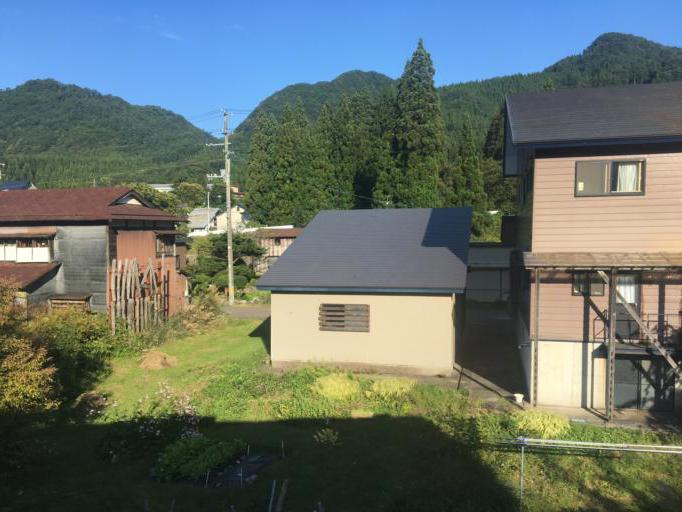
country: JP
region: Akita
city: Takanosu
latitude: 39.9941
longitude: 140.4011
